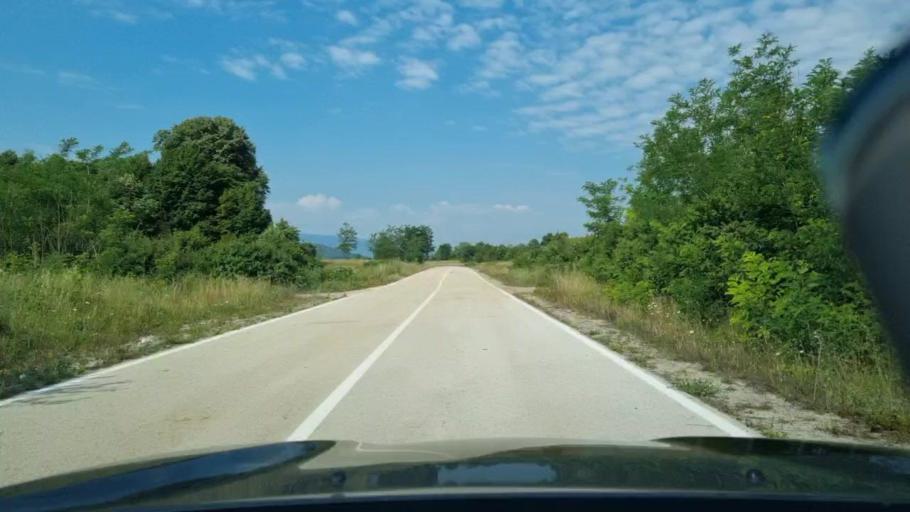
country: BA
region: Federation of Bosnia and Herzegovina
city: Ostrozac
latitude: 44.8934
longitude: 15.9682
